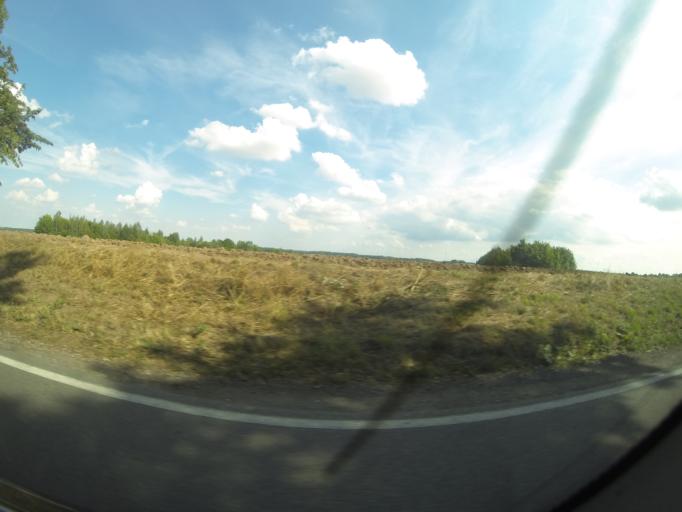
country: DE
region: Thuringia
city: Vollmershain
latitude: 50.8685
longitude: 12.3044
